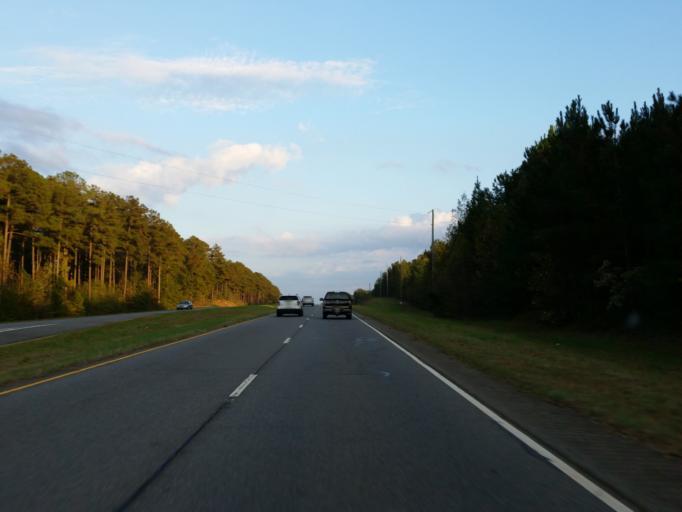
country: US
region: Georgia
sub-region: Houston County
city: Perry
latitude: 32.4159
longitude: -83.6909
